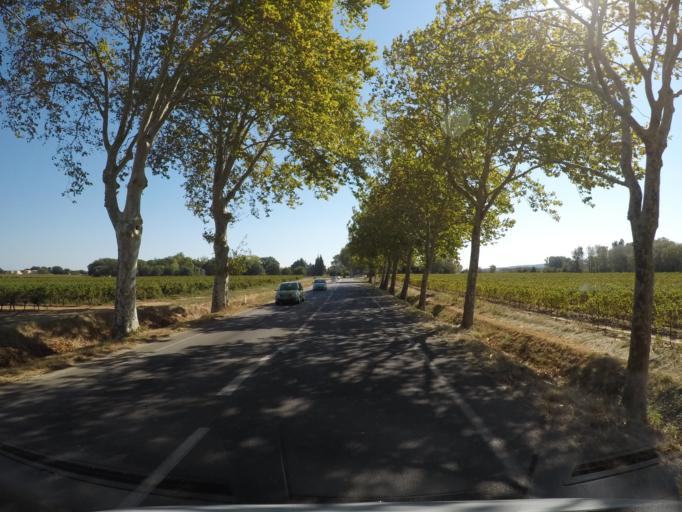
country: FR
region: Languedoc-Roussillon
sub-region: Departement du Gard
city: Castillon-du-Gard
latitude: 43.9739
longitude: 4.4932
